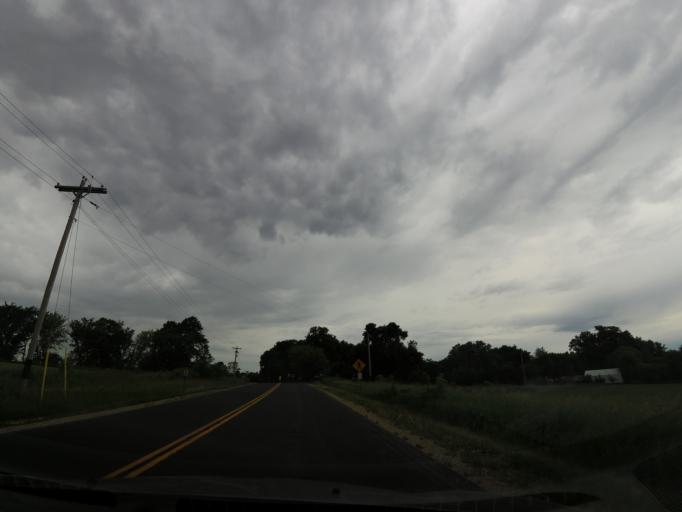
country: US
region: Minnesota
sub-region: Scott County
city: Prior Lake
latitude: 44.6949
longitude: -93.4231
